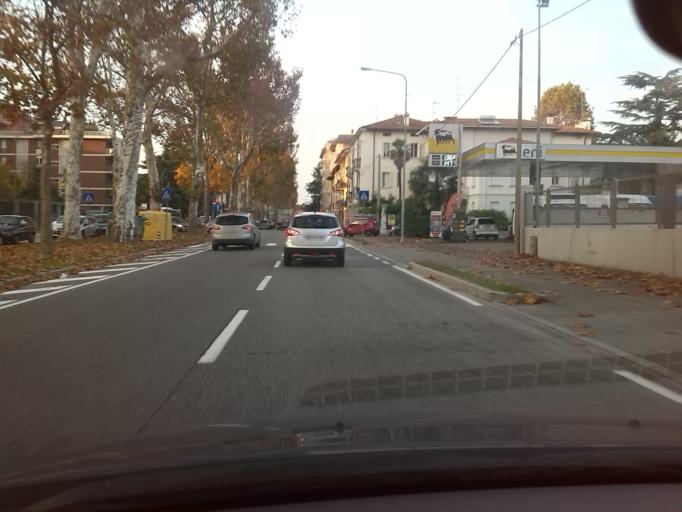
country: IT
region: Friuli Venezia Giulia
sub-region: Provincia di Udine
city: Udine
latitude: 46.0590
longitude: 13.2482
